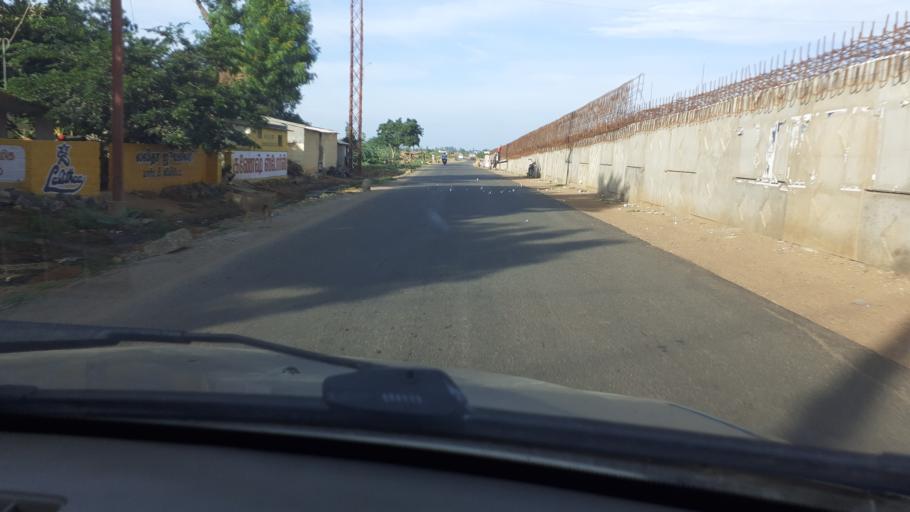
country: IN
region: Tamil Nadu
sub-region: Tirunelveli Kattabo
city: Tirunelveli
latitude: 8.6277
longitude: 77.6962
